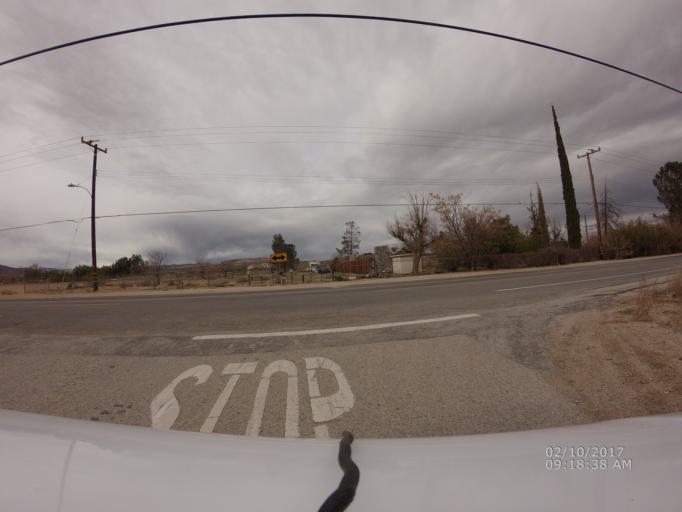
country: US
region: California
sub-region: Los Angeles County
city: Littlerock
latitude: 34.4937
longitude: -117.8965
